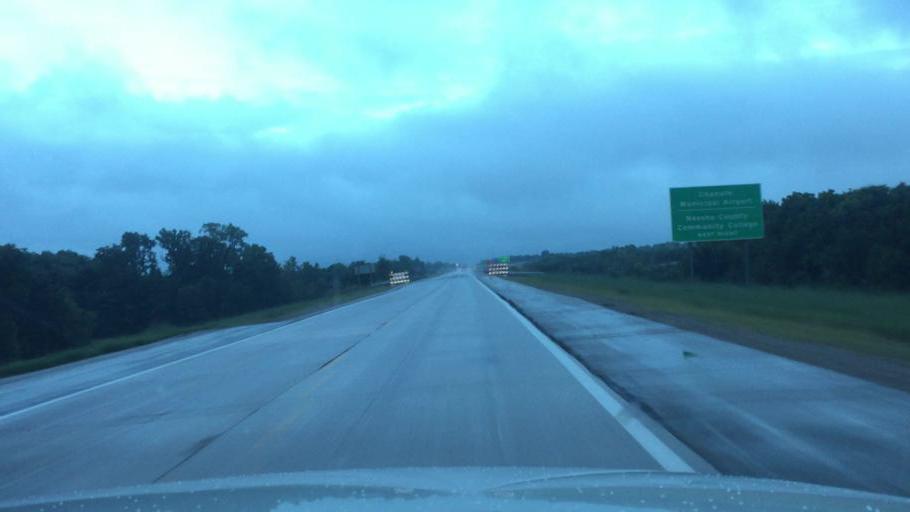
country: US
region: Kansas
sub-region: Neosho County
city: Chanute
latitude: 37.7018
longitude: -95.4795
